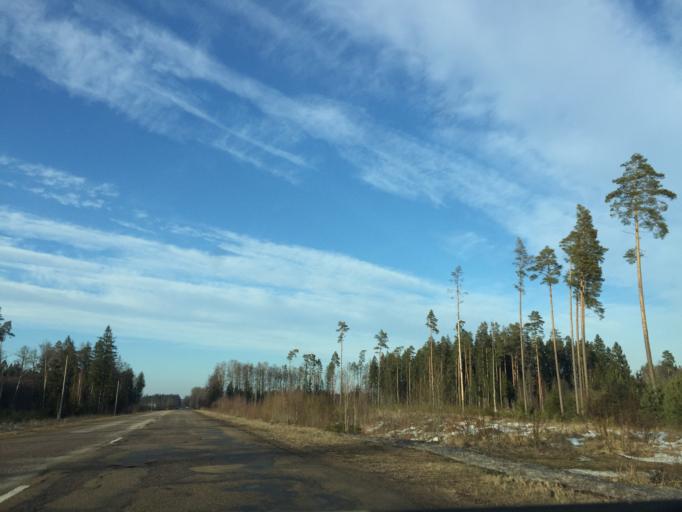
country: LV
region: Kekava
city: Balozi
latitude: 56.7259
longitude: 24.1105
